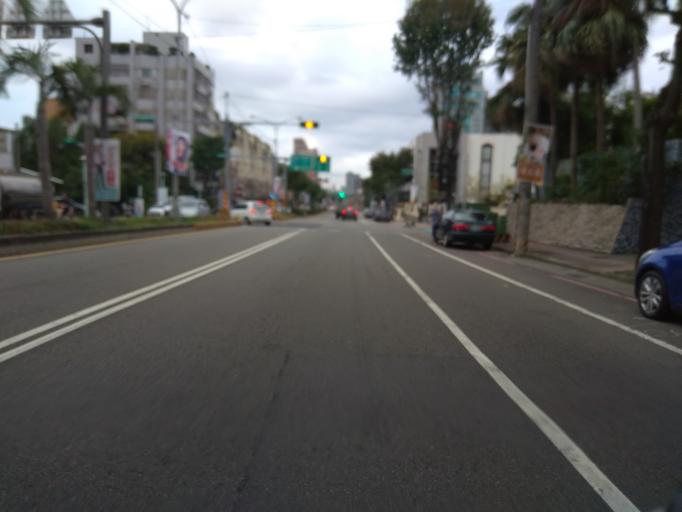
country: TW
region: Taiwan
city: Daxi
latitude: 24.9426
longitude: 121.2066
